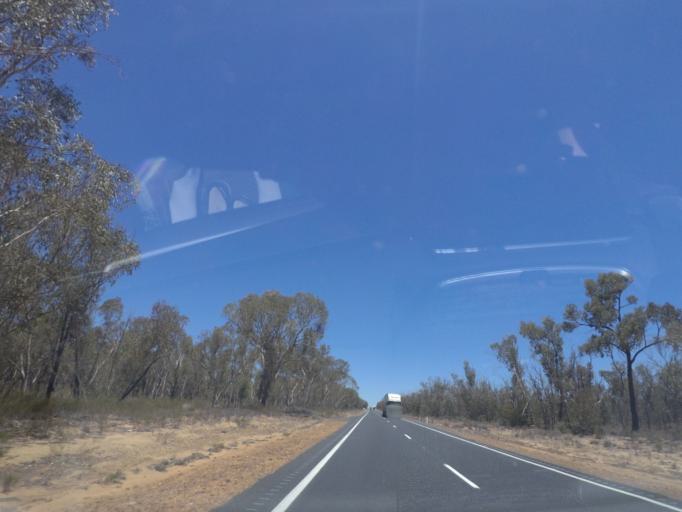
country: AU
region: New South Wales
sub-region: Warrumbungle Shire
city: Coonabarabran
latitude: -30.9546
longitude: 149.4207
